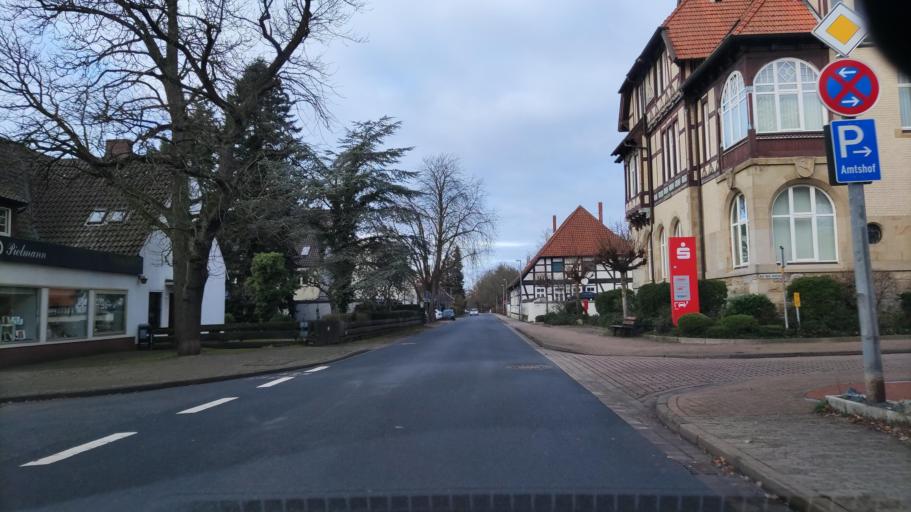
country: DE
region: Lower Saxony
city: Isernhagen Farster Bauerschaft
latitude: 52.4926
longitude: 9.8557
